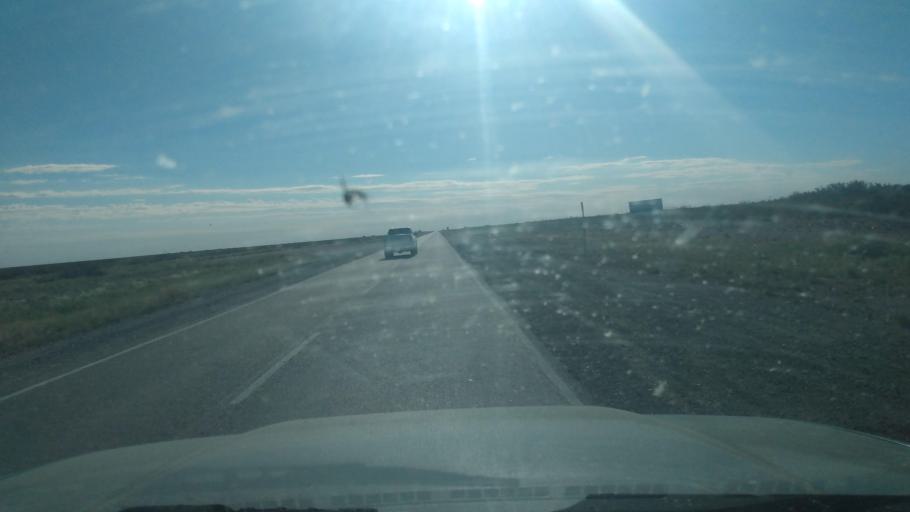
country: AR
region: La Pampa
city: Veinticinco de Mayo
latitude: -37.6603
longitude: -67.7431
